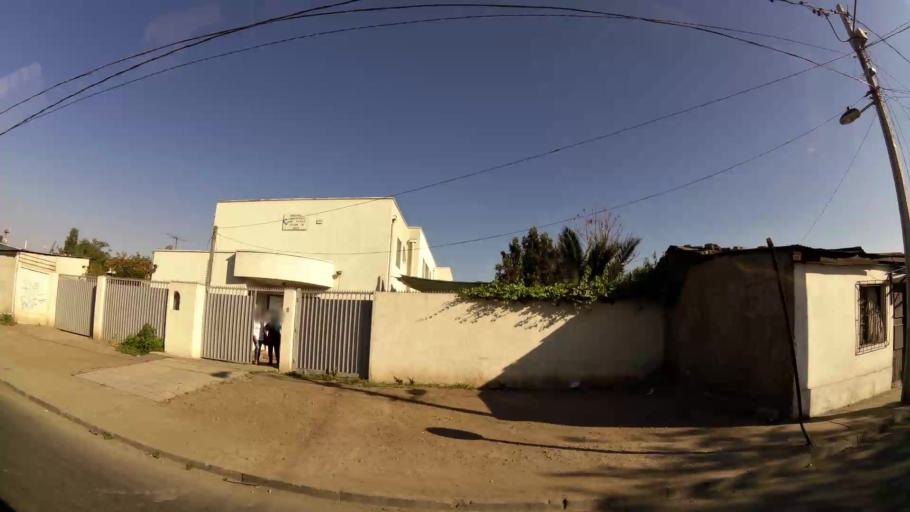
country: CL
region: Santiago Metropolitan
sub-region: Provincia de Santiago
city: La Pintana
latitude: -33.5475
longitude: -70.6320
